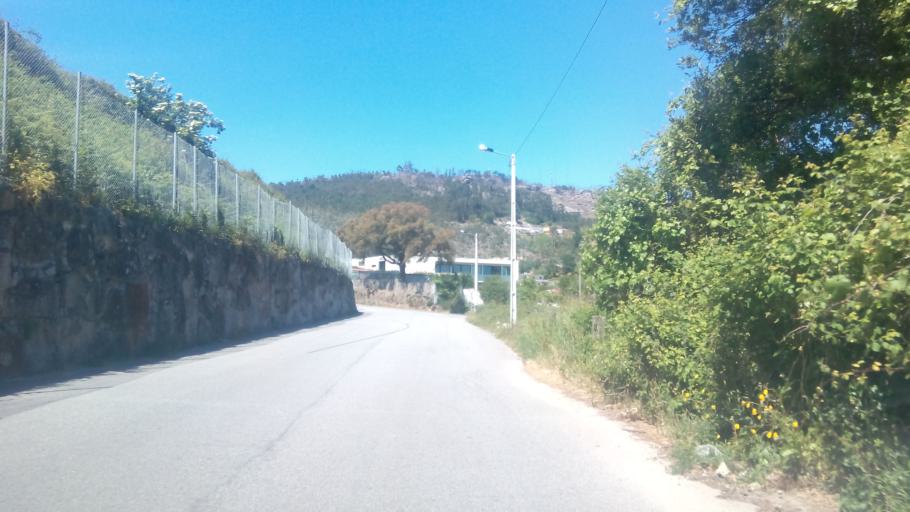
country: PT
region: Porto
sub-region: Paredes
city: Baltar
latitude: 41.1878
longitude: -8.3933
